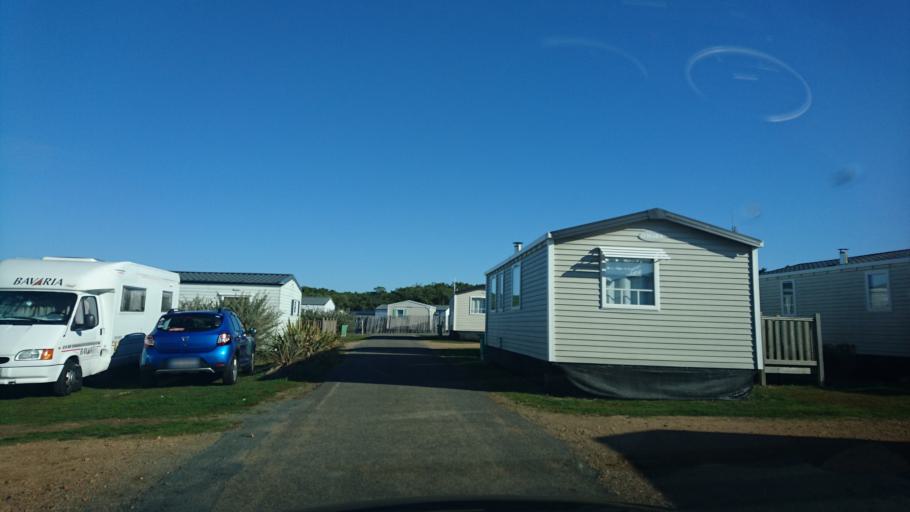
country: FR
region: Pays de la Loire
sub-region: Departement de la Vendee
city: Les Sables-d'Olonne
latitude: 46.5126
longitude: -1.8152
